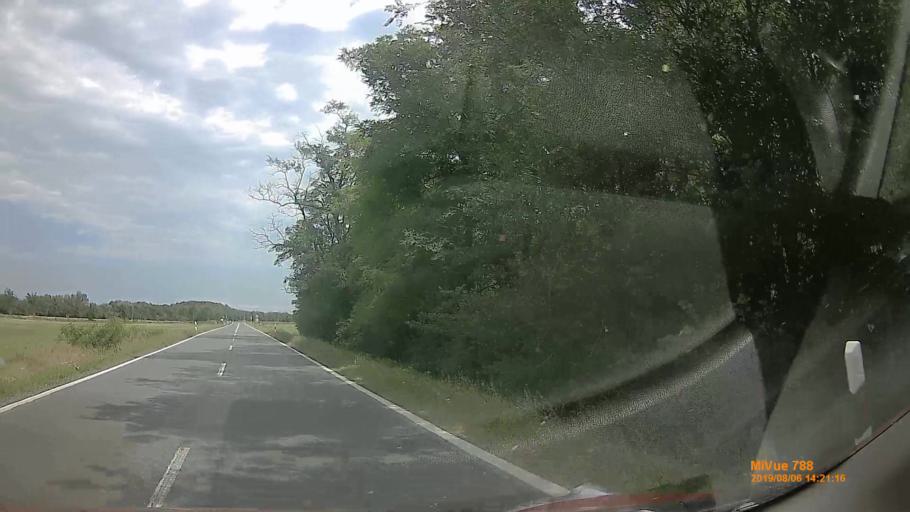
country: HU
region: Vas
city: Vep
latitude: 47.1704
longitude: 16.7720
